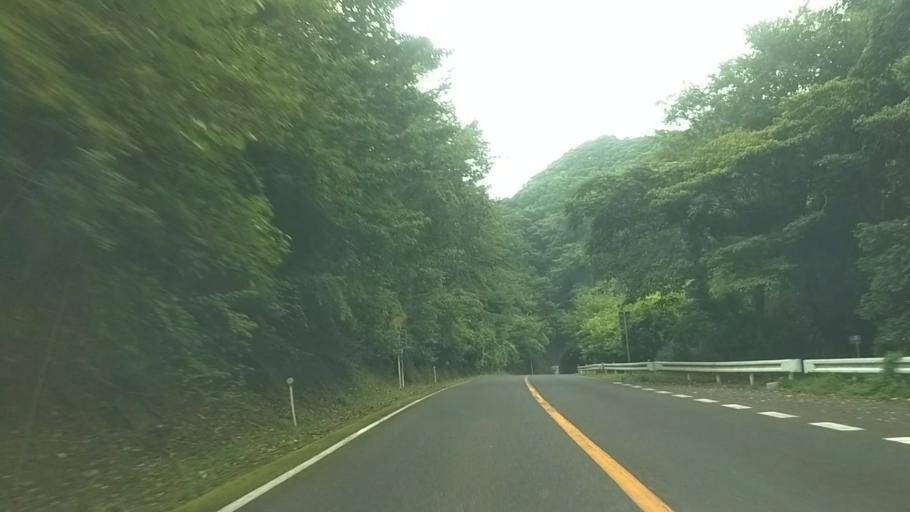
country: JP
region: Chiba
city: Kawaguchi
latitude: 35.2230
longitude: 140.0360
